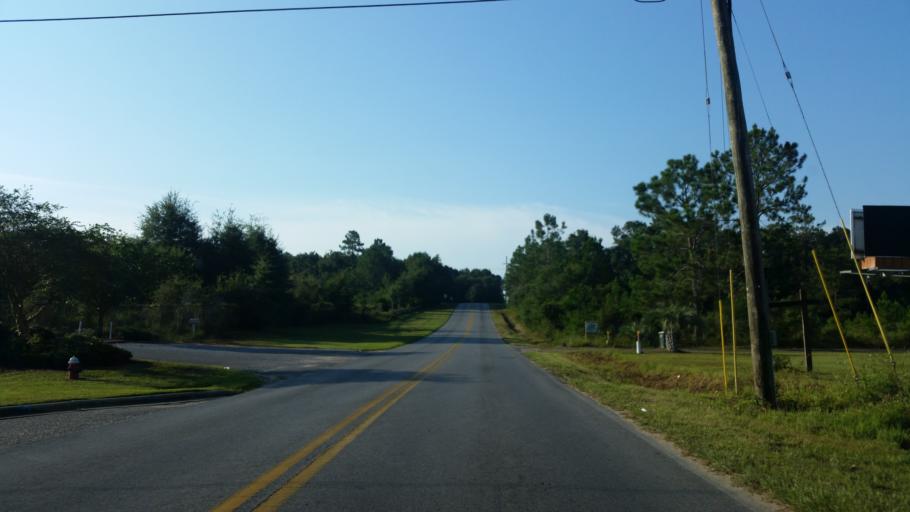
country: US
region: Florida
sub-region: Santa Rosa County
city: Bagdad
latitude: 30.6042
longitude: -87.0647
